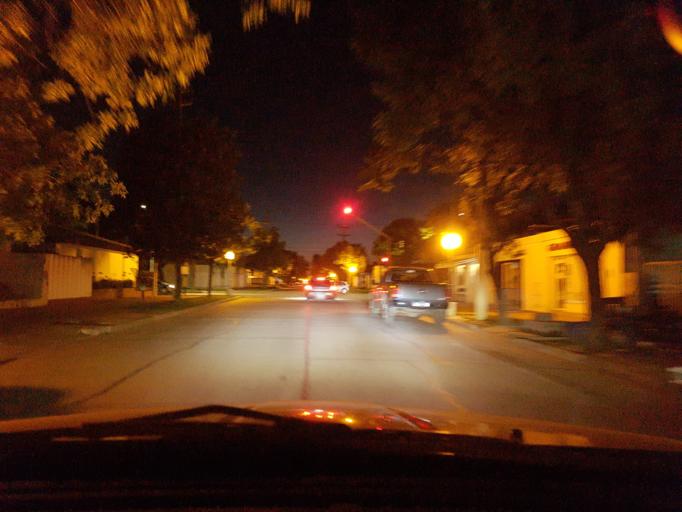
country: AR
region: Cordoba
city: General Cabrera
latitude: -32.7581
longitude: -63.7925
